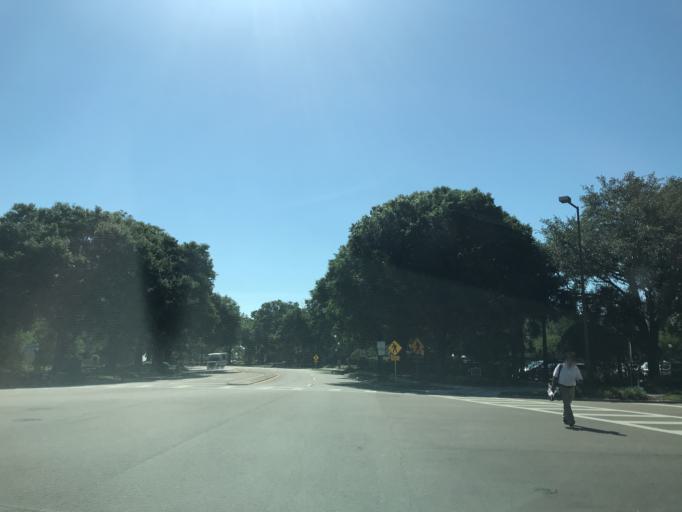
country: US
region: Florida
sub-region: Osceola County
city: Celebration
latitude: 28.3683
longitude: -81.5065
